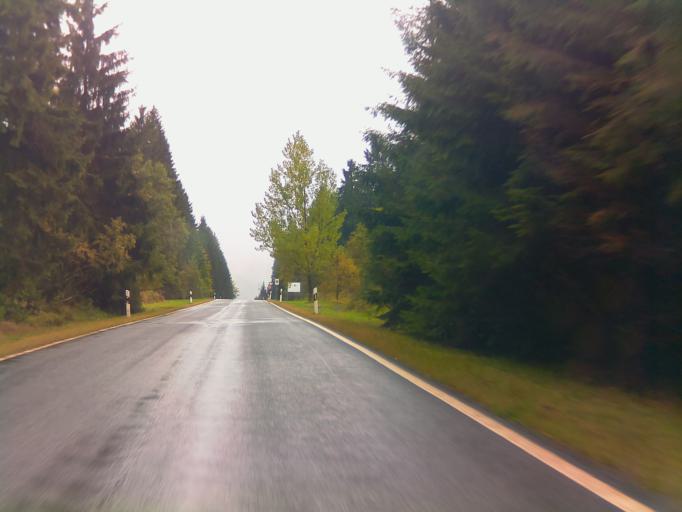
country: DE
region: Bavaria
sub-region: Upper Franconia
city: Tschirn
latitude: 50.4336
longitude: 11.4675
